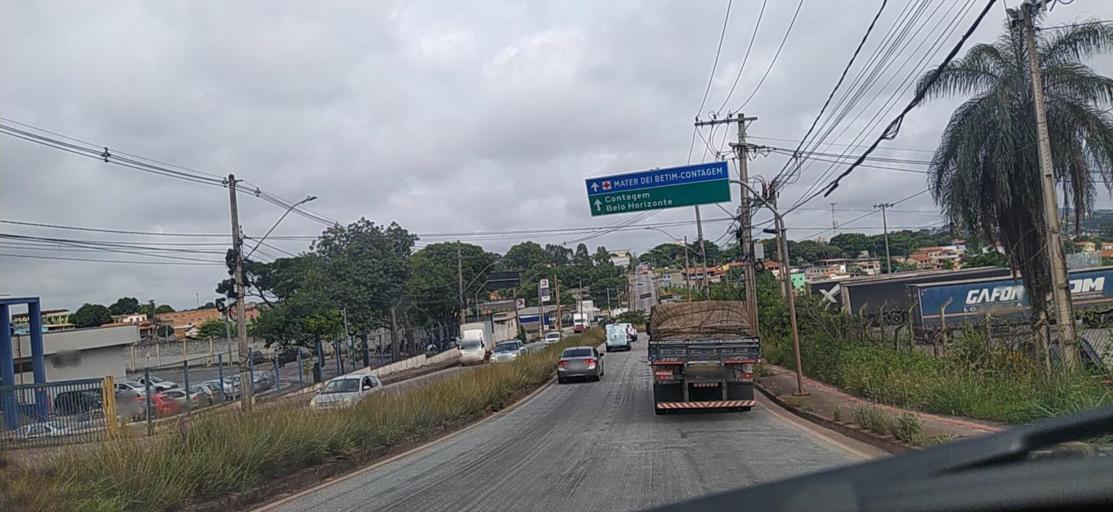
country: BR
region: Minas Gerais
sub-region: Betim
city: Betim
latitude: -19.9539
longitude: -44.1508
